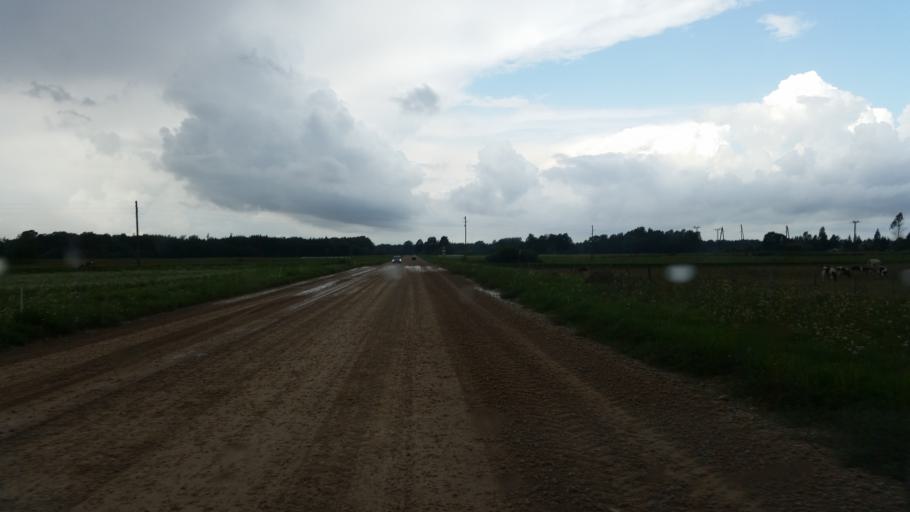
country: LV
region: Vecumnieki
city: Vecumnieki
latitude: 56.4282
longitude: 24.4626
